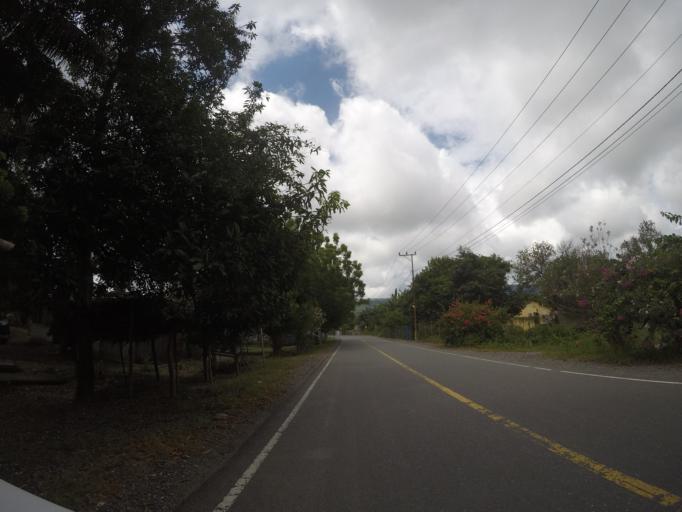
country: TL
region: Liquica
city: Maubara
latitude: -8.7326
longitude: 125.1361
